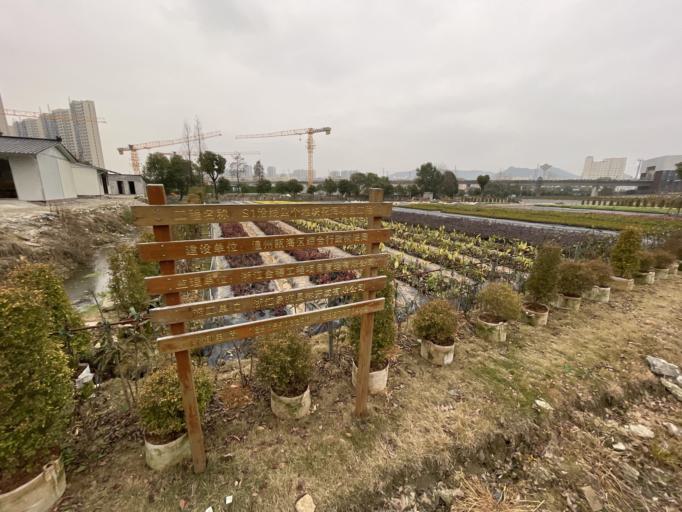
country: CN
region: Zhejiang Sheng
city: Louqiao
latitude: 27.9788
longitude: 120.6223
